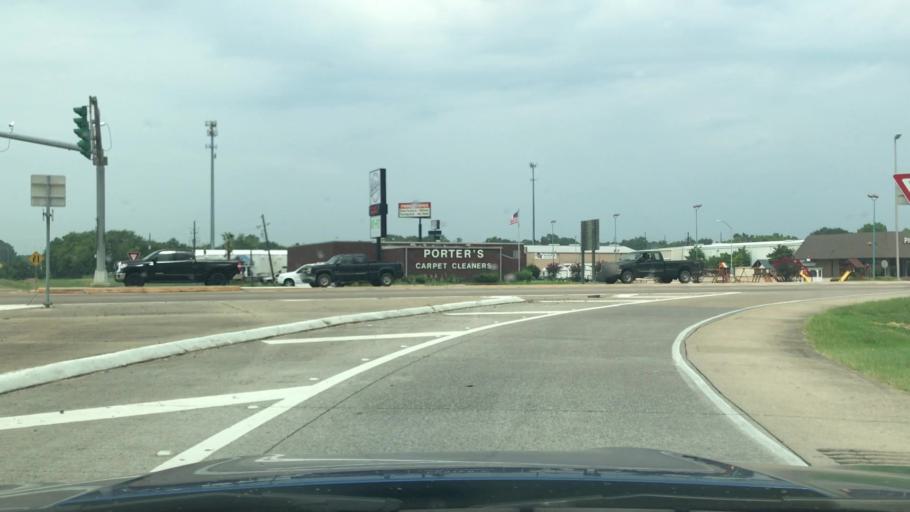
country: US
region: Louisiana
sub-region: Bossier Parish
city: Bossier City
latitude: 32.4122
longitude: -93.7241
